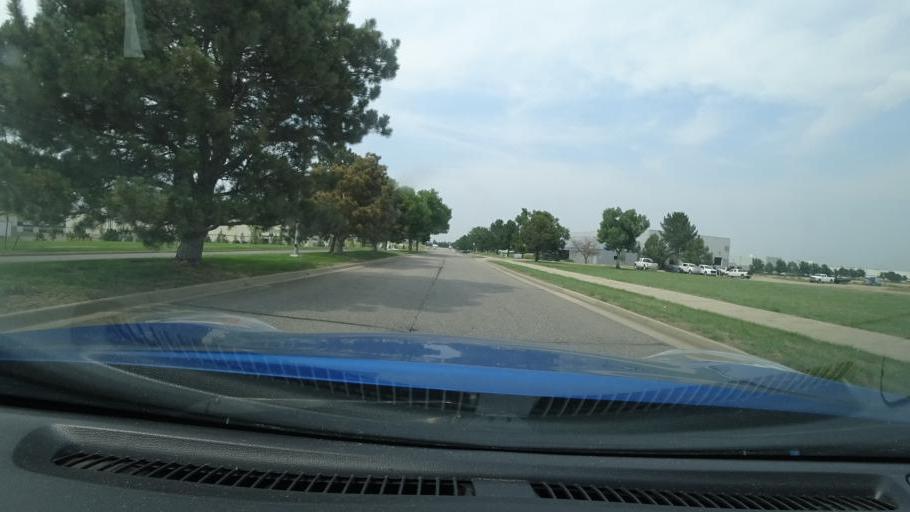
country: US
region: Colorado
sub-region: Adams County
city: Aurora
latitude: 39.7607
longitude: -104.7528
